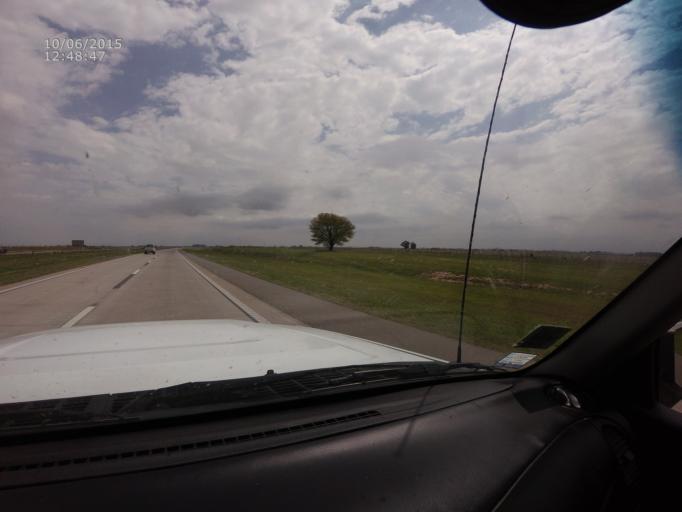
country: AR
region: Santa Fe
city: Canada de Gomez
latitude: -32.8364
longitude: -61.4568
